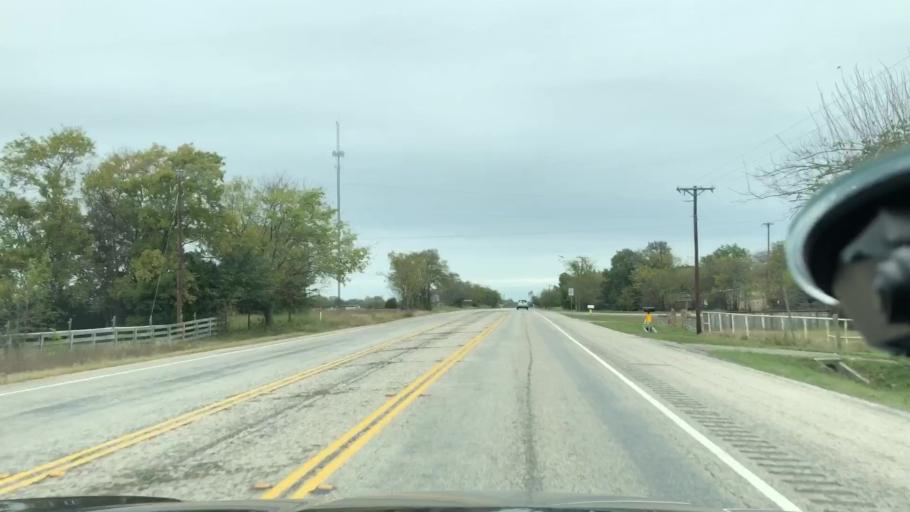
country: US
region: Texas
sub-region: Hunt County
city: Quinlan
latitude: 32.9765
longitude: -96.1086
